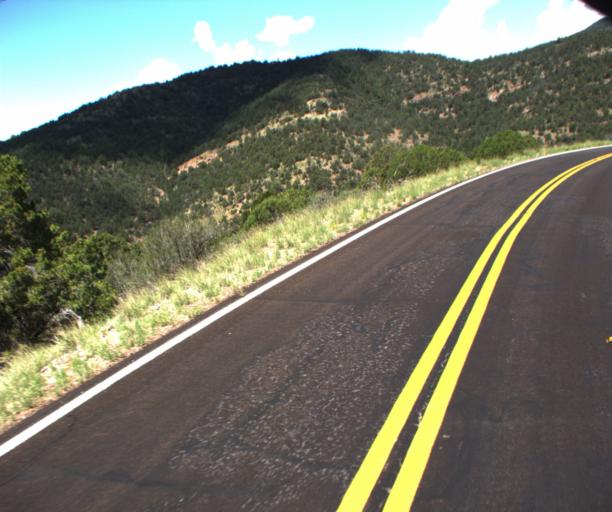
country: US
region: Arizona
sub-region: Greenlee County
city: Morenci
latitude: 33.4016
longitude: -109.3485
